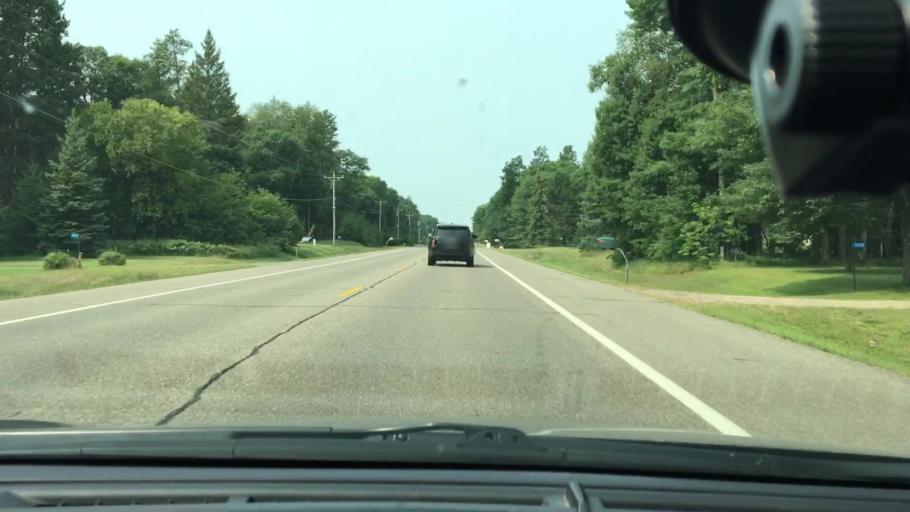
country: US
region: Minnesota
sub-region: Crow Wing County
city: Brainerd
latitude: 46.3985
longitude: -94.1970
